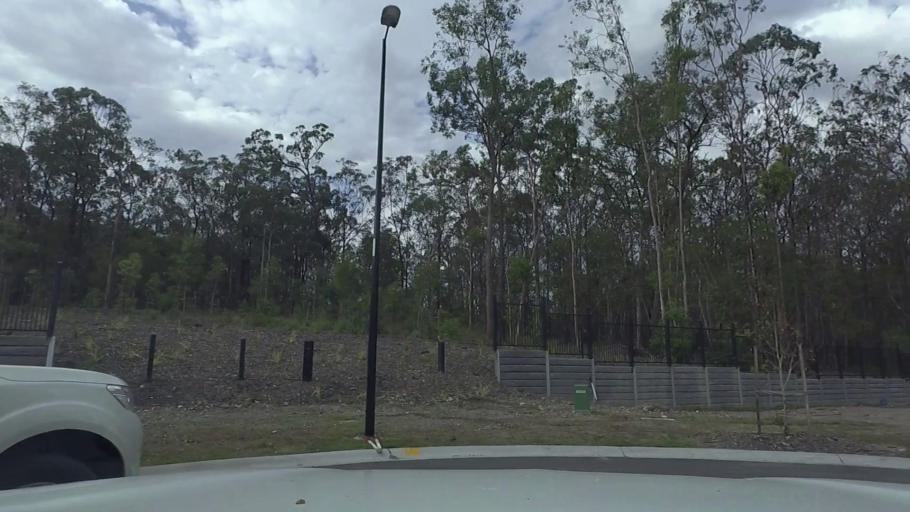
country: AU
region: Queensland
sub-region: Logan
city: Windaroo
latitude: -27.7283
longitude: 153.1676
